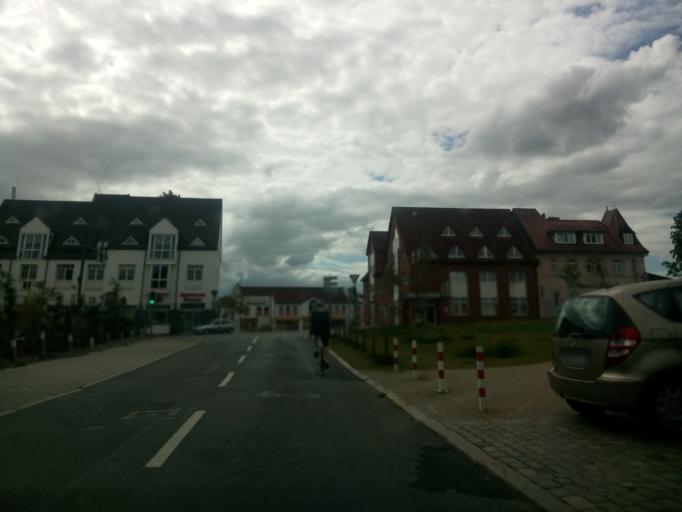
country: DE
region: Lower Saxony
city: Ritterhude
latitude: 53.1563
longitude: 8.7052
